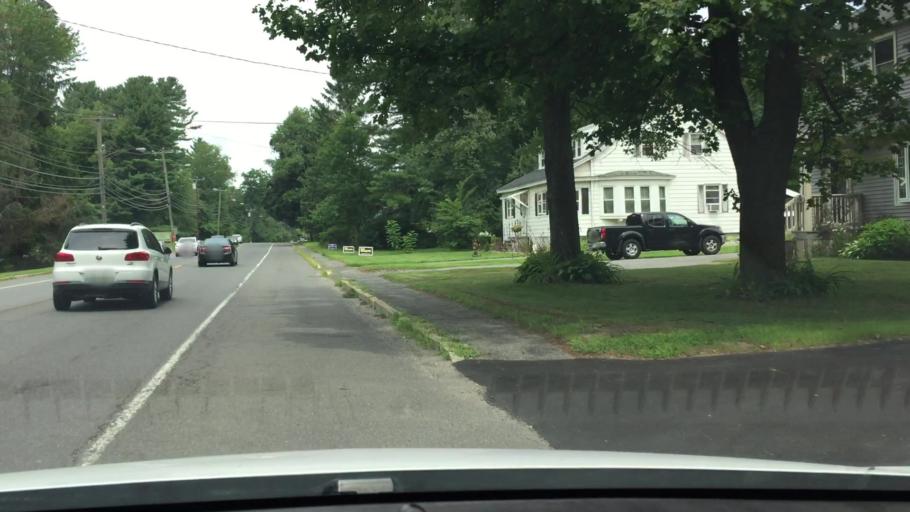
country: US
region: Massachusetts
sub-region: Berkshire County
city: Dalton
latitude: 42.4755
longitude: -73.2046
